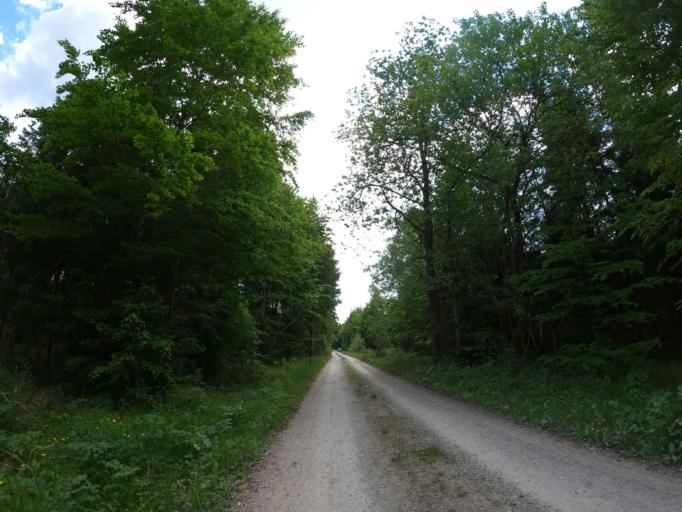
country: DE
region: Bavaria
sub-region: Upper Bavaria
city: Sauerlach
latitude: 47.9770
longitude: 11.6790
